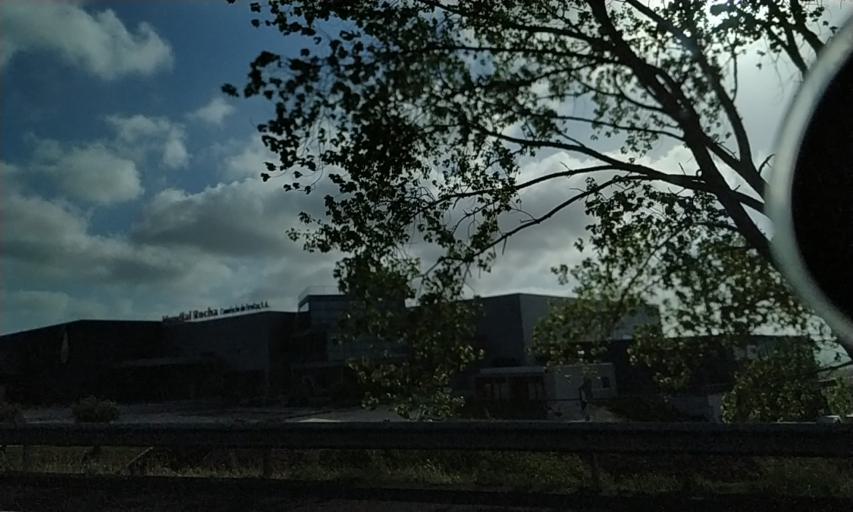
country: PT
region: Leiria
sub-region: Obidos
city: Obidos
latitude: 39.3349
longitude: -9.1744
